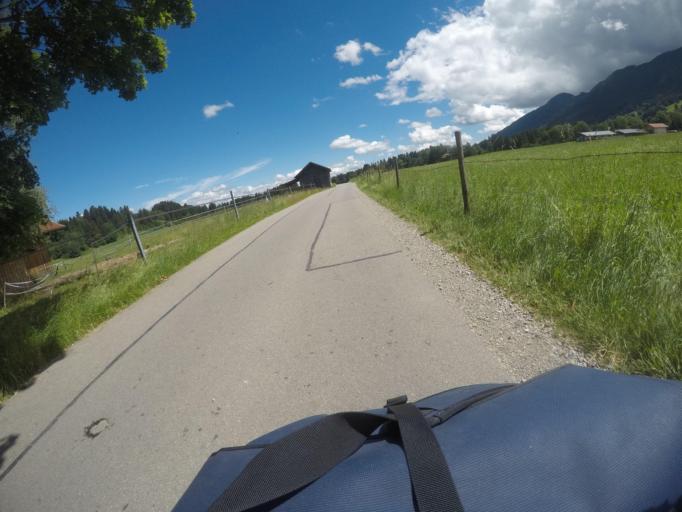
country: DE
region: Bavaria
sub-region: Swabia
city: Halblech
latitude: 47.6288
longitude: 10.8100
